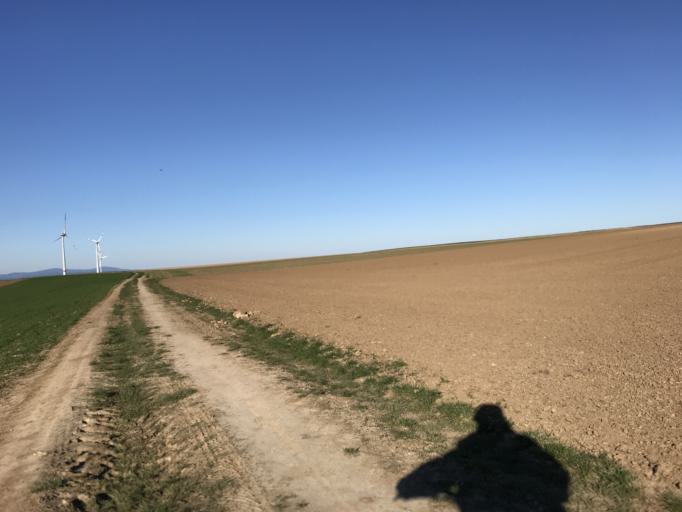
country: DE
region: Rheinland-Pfalz
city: Klein-Winternheim
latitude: 49.9265
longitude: 8.2340
